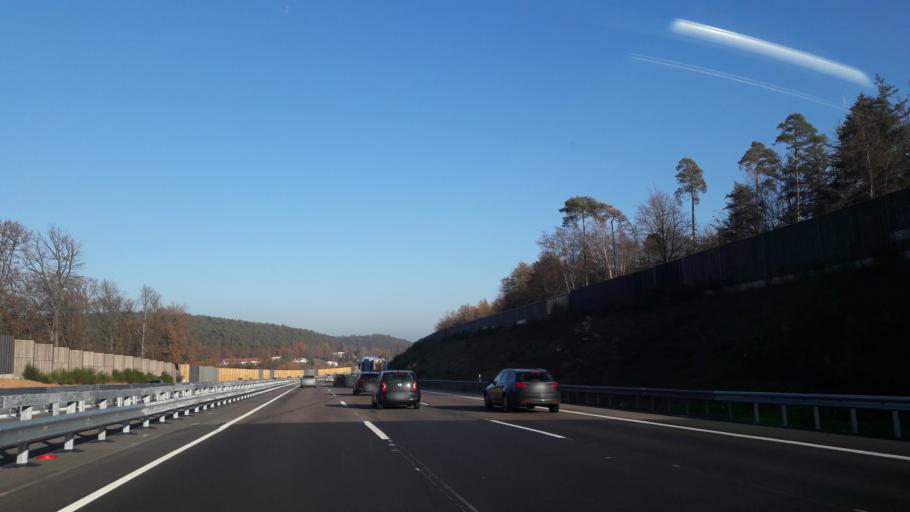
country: DE
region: Rheinland-Pfalz
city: Otterbach
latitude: 49.4524
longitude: 7.7366
